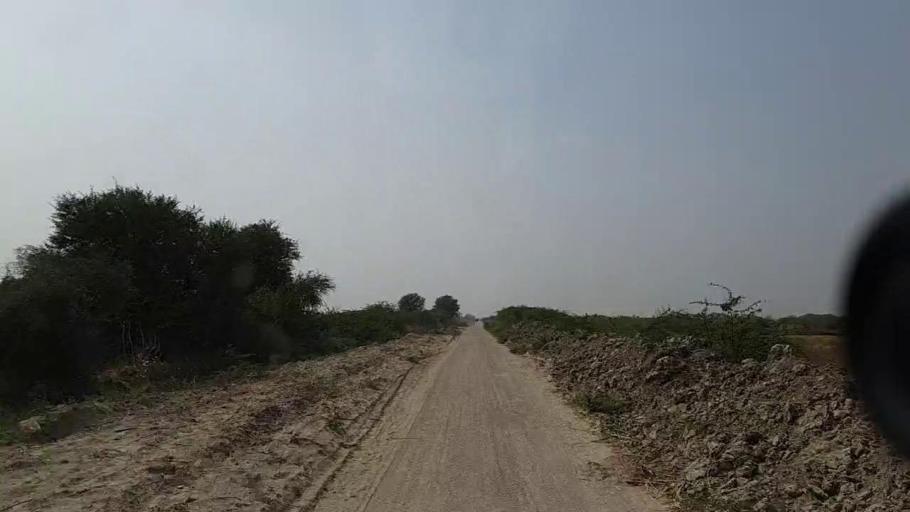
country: PK
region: Sindh
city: Naukot
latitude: 24.7707
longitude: 69.3308
